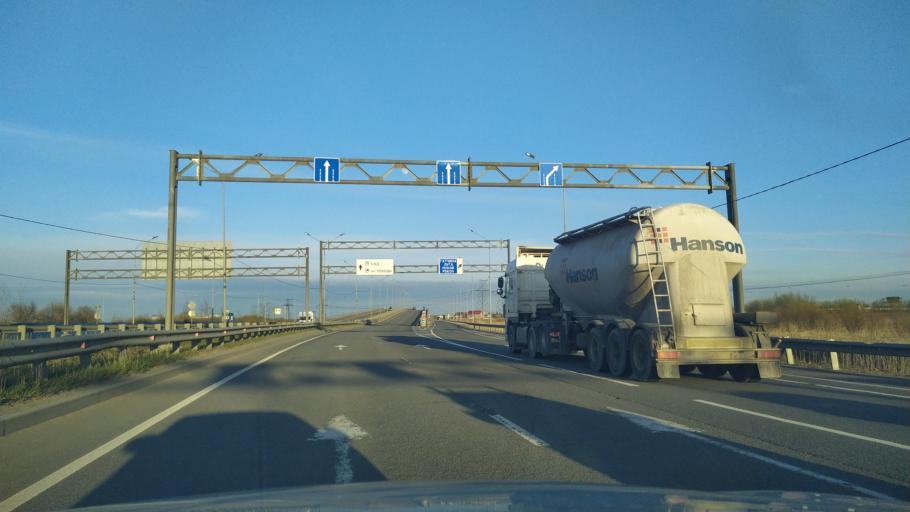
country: RU
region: St.-Petersburg
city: Aleksandrovskaya
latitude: 59.7469
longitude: 30.3027
